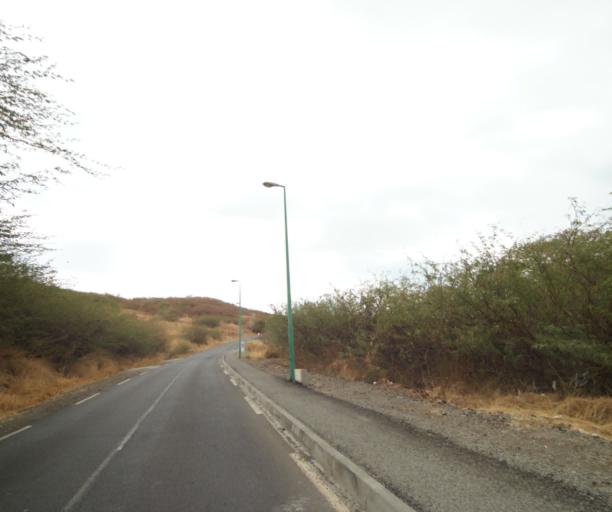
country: RE
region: Reunion
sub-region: Reunion
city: Saint-Paul
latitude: -21.0595
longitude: 55.2326
